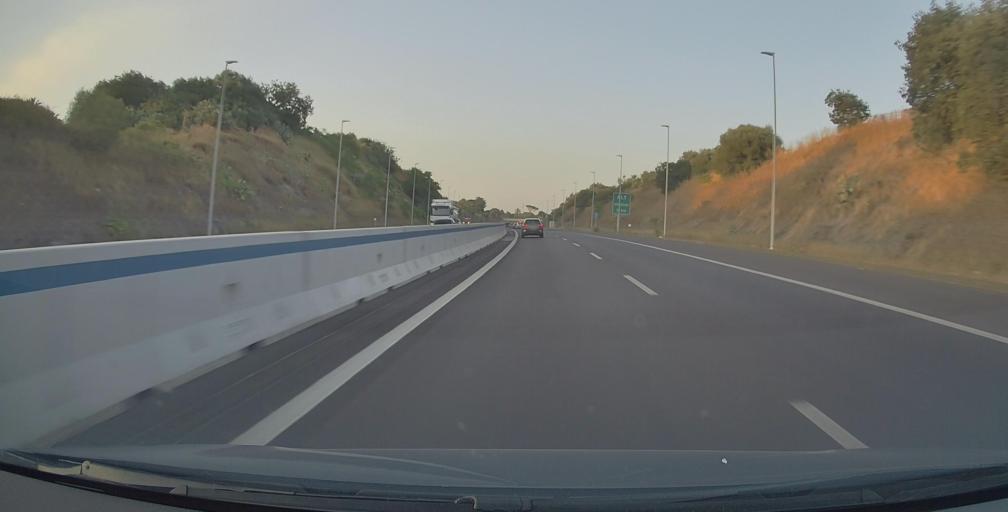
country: IT
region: Sicily
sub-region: Catania
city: Sant'Agata Li Battiati
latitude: 37.5540
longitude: 15.0855
